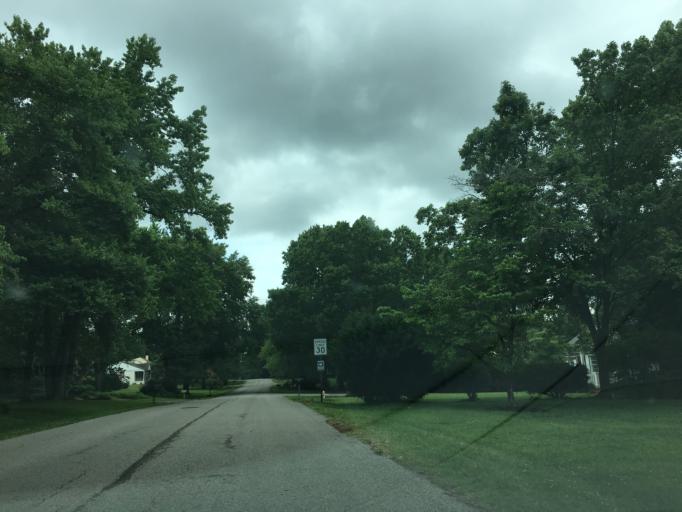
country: US
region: Tennessee
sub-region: Davidson County
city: Oak Hill
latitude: 36.1057
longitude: -86.7766
